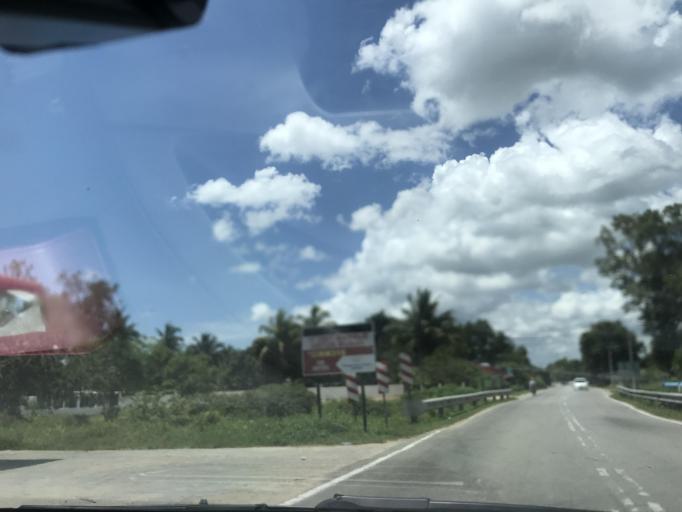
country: MY
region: Kelantan
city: Tumpat
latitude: 6.1875
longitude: 102.1618
